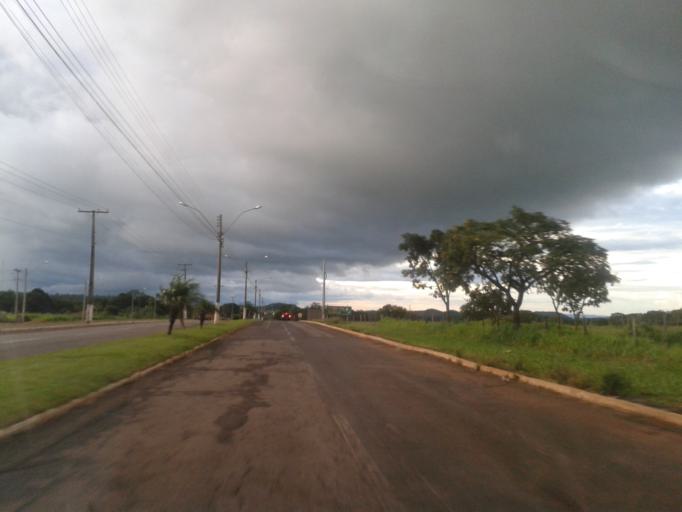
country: BR
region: Goias
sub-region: Morrinhos
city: Morrinhos
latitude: -17.7325
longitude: -49.1444
